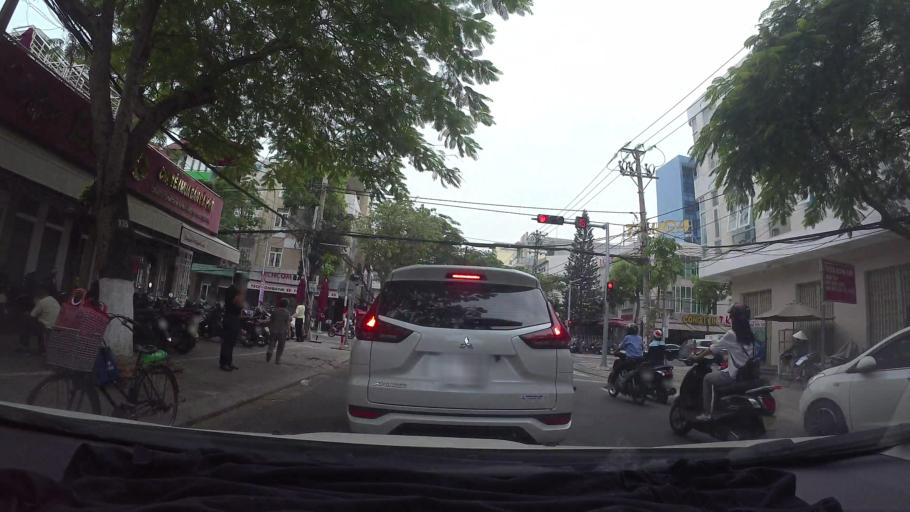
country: VN
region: Da Nang
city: Da Nang
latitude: 16.0750
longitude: 108.2199
